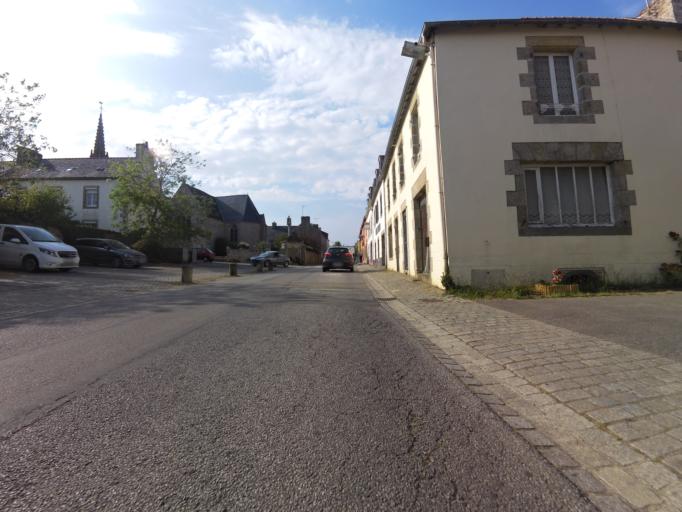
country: FR
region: Brittany
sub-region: Departement du Finistere
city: Pouldreuzic
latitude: 47.9534
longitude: -4.3592
